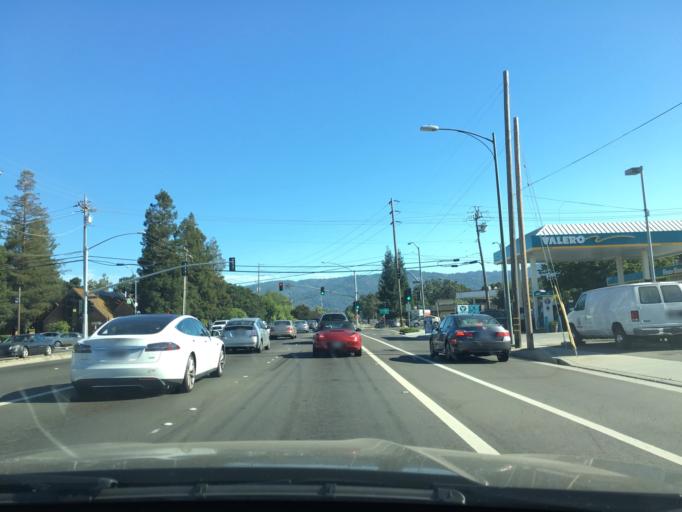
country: US
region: California
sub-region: Santa Clara County
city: Cupertino
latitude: 37.2947
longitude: -122.0324
